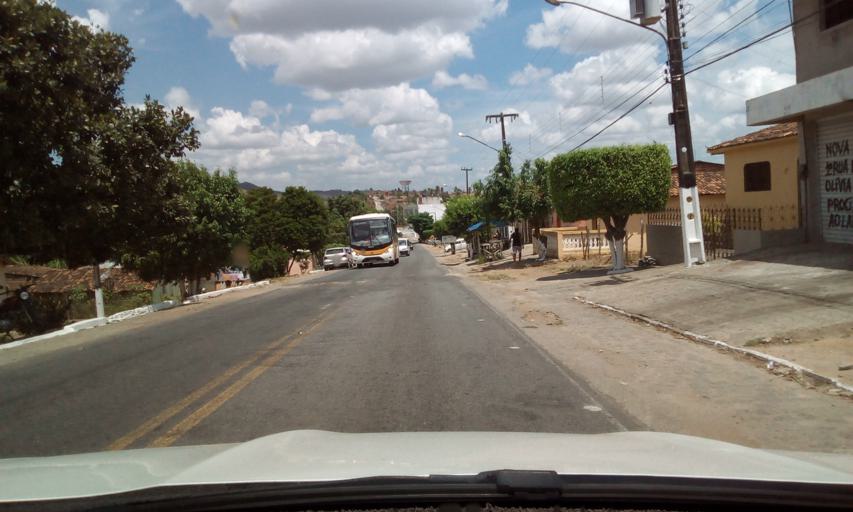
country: BR
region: Paraiba
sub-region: Alagoinha
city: Alagoinha
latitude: -6.9026
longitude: -35.5263
